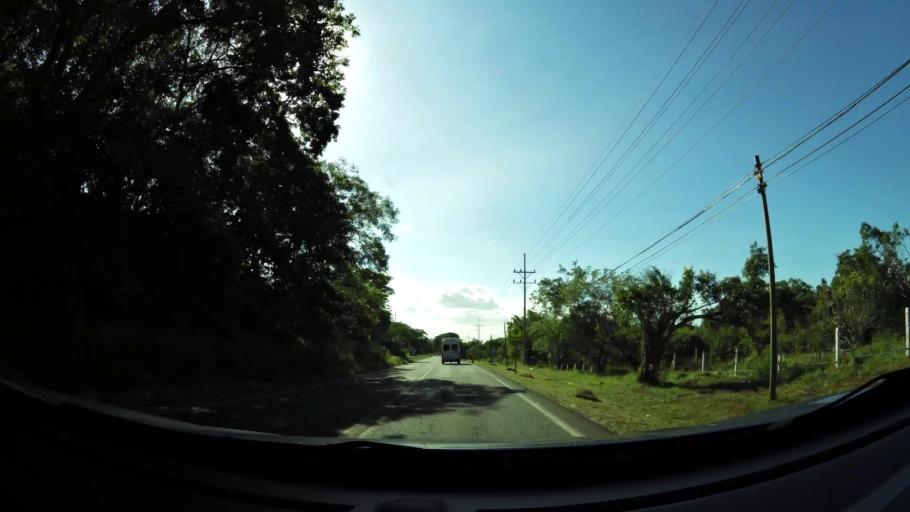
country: CR
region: Guanacaste
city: Sardinal
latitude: 10.5804
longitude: -85.5738
